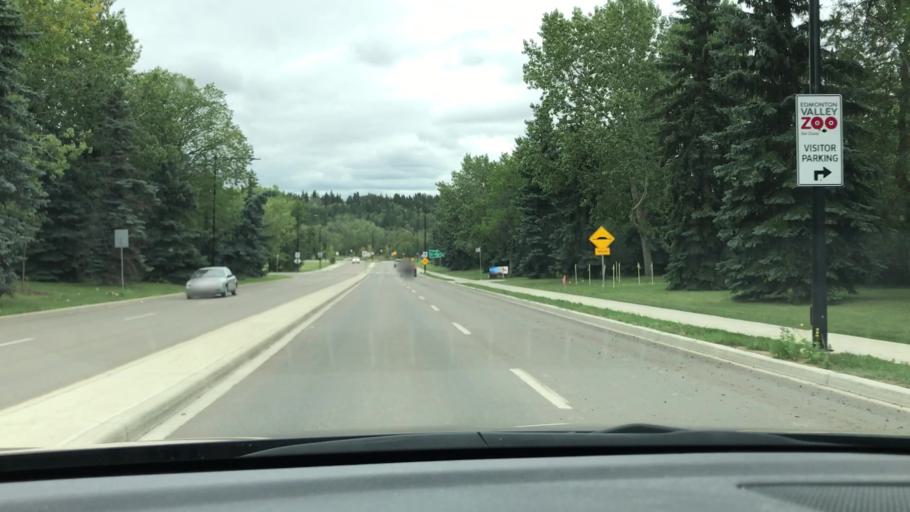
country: CA
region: Alberta
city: Edmonton
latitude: 53.5131
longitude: -113.5535
